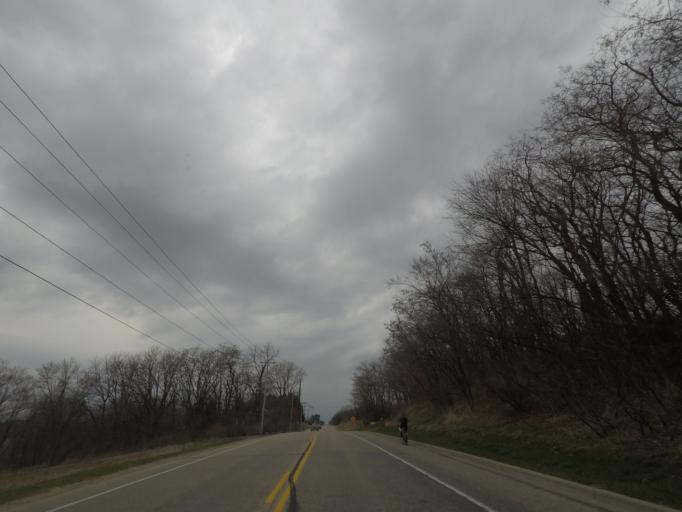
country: US
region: Wisconsin
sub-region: Dane County
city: Middleton
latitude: 43.1110
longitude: -89.5719
